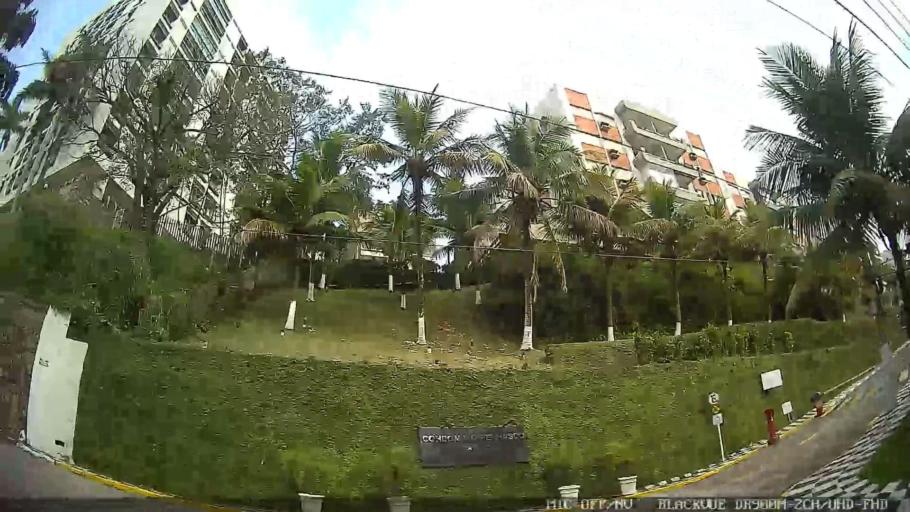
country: BR
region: Sao Paulo
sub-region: Guaruja
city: Guaruja
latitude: -23.9926
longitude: -46.1971
